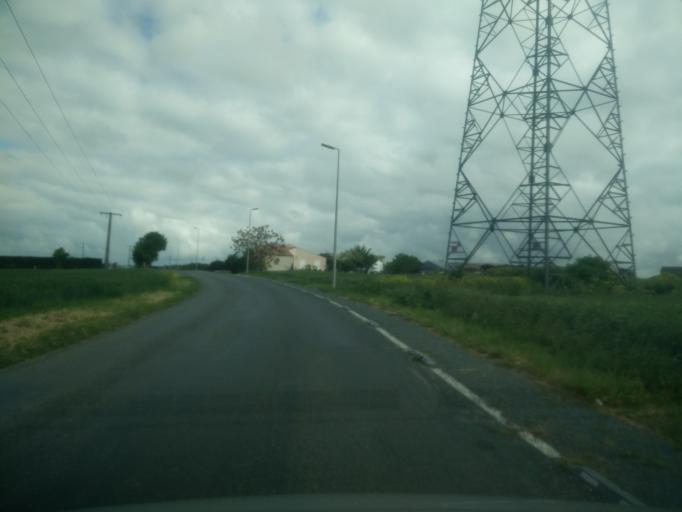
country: FR
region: Poitou-Charentes
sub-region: Departement de la Charente-Maritime
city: Puilboreau
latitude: 46.1912
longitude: -1.1189
